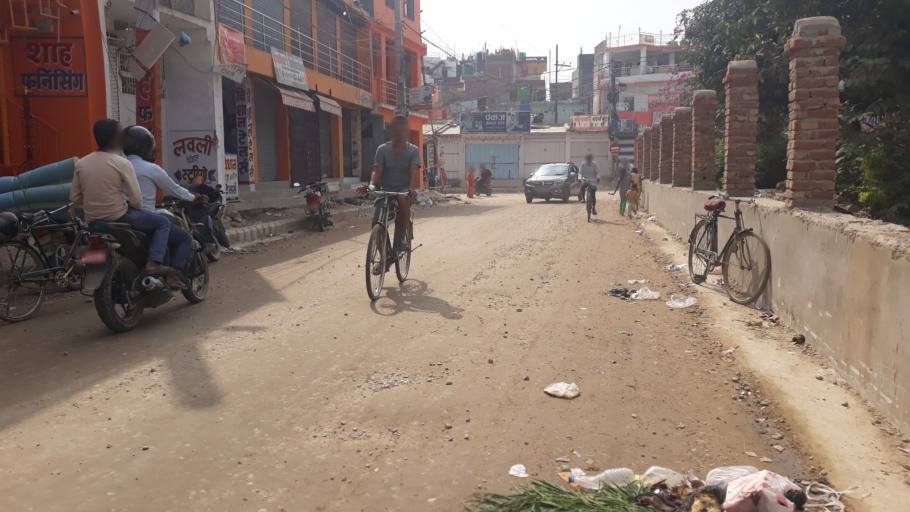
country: NP
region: Central Region
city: Janakpur
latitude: 26.7303
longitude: 85.9269
